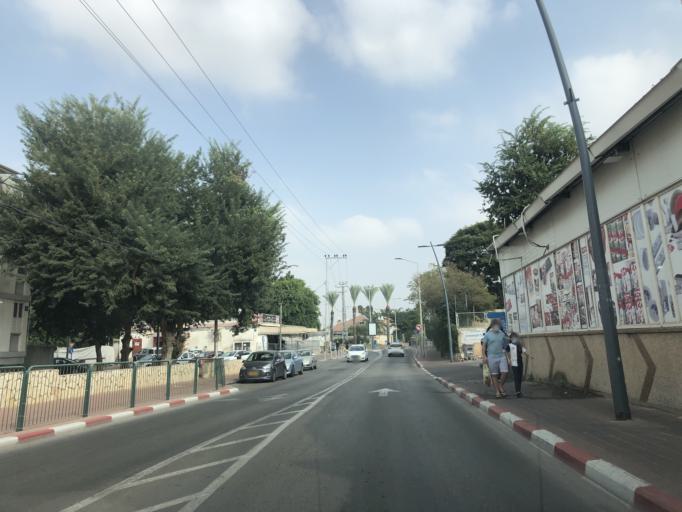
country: IL
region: Central District
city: Rosh Ha'Ayin
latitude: 32.0962
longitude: 34.9463
